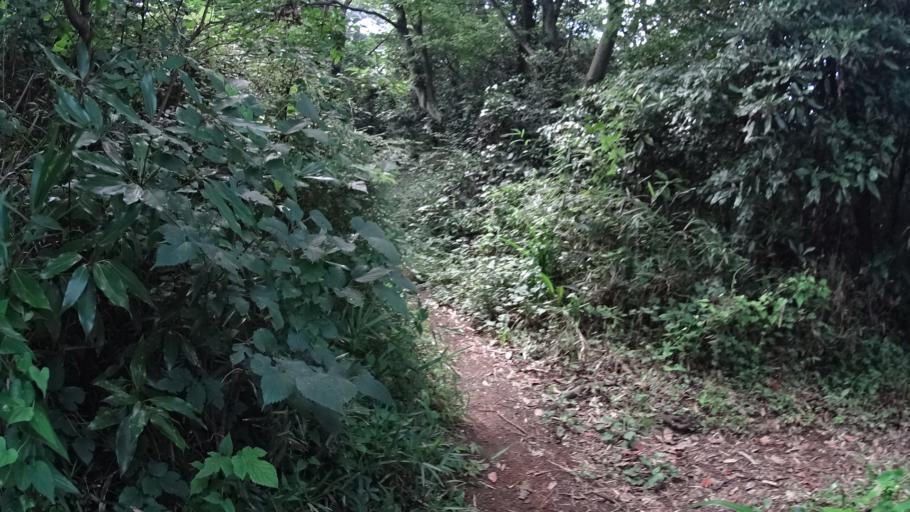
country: JP
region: Kanagawa
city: Zushi
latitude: 35.3116
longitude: 139.6109
